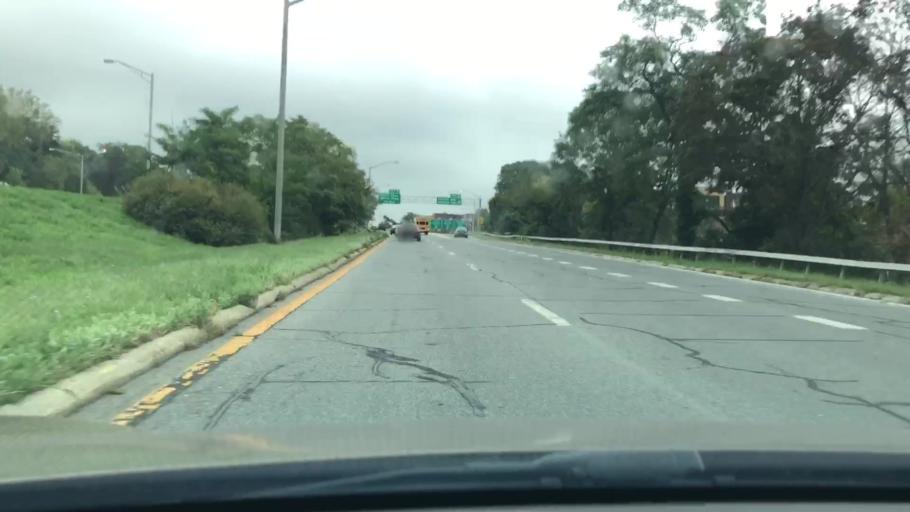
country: US
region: New York
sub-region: Westchester County
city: Bronxville
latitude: 40.9300
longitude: -73.8523
